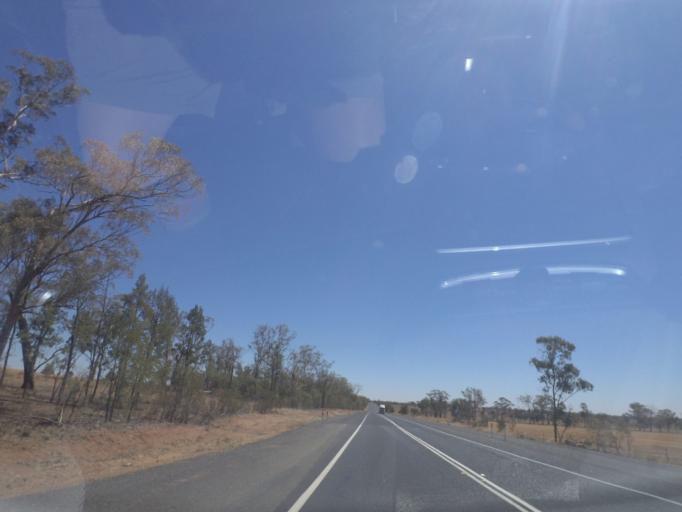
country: AU
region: New South Wales
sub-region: Gilgandra
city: Gilgandra
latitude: -31.4871
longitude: 148.8778
